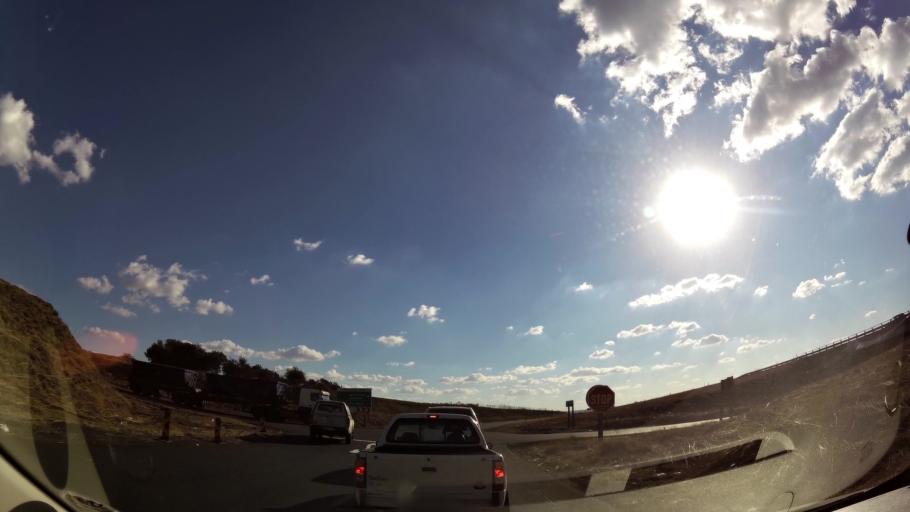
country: ZA
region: Mpumalanga
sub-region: Nkangala District Municipality
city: Witbank
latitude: -25.8805
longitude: 29.1646
